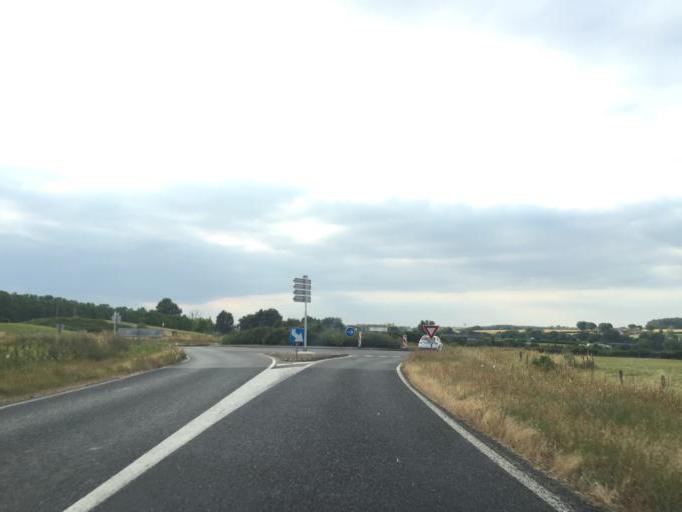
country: FR
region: Auvergne
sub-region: Departement de l'Allier
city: Toulon-sur-Allier
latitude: 46.5374
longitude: 3.3837
